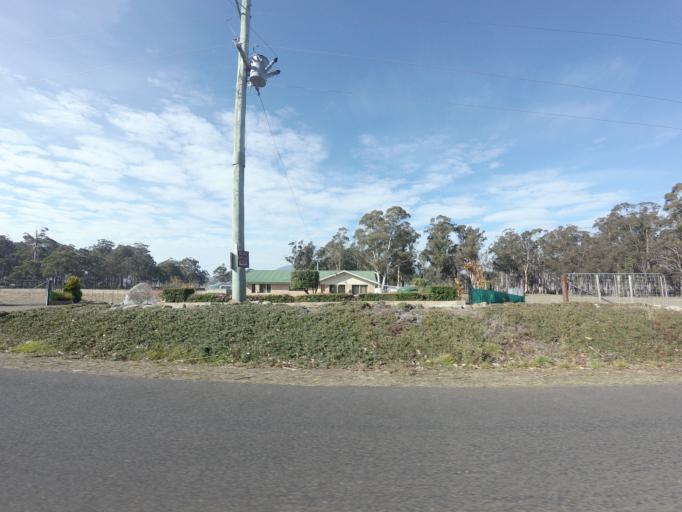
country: AU
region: Tasmania
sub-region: Sorell
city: Sorell
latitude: -42.4639
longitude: 147.4613
